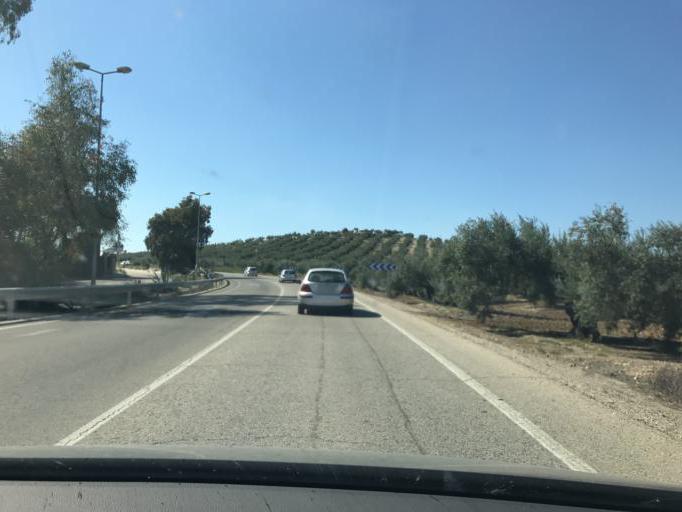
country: ES
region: Andalusia
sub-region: Province of Cordoba
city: Luque
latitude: 37.5719
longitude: -4.2536
